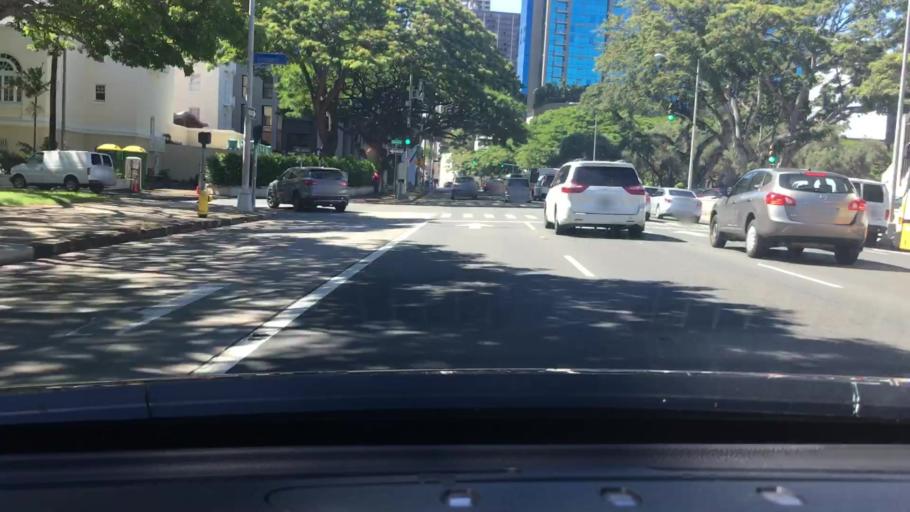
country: US
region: Hawaii
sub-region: Honolulu County
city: Honolulu
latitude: 21.3086
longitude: -157.8574
